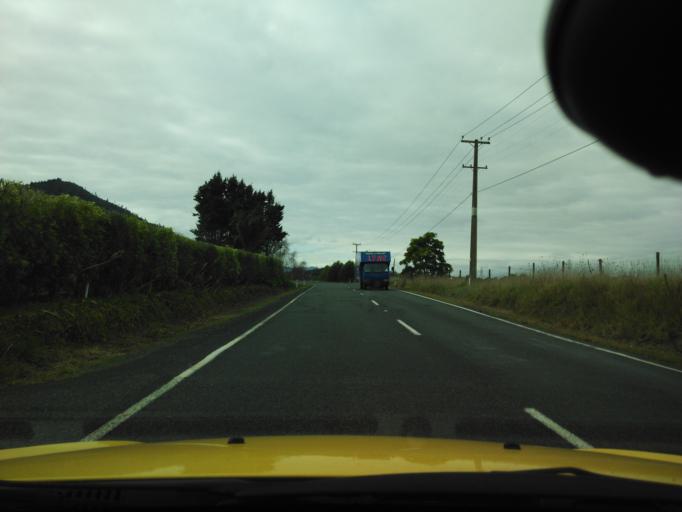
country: NZ
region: Waikato
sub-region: Waikato District
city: Ngaruawahia
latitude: -37.6203
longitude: 175.1777
